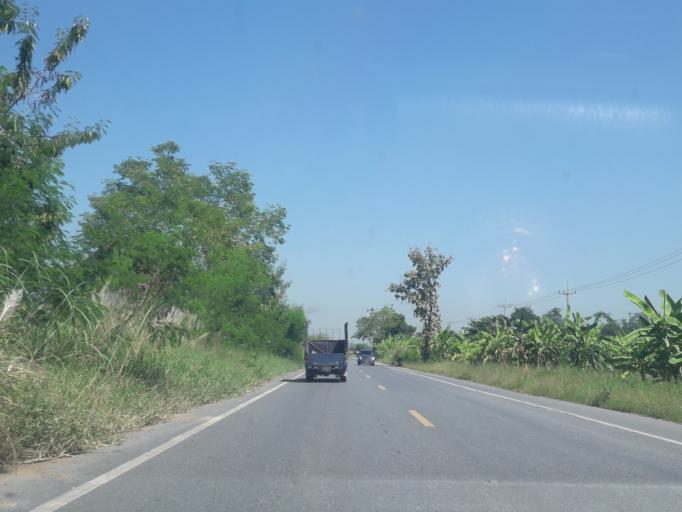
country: TH
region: Sara Buri
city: Nong Khae
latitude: 14.2578
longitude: 100.8233
